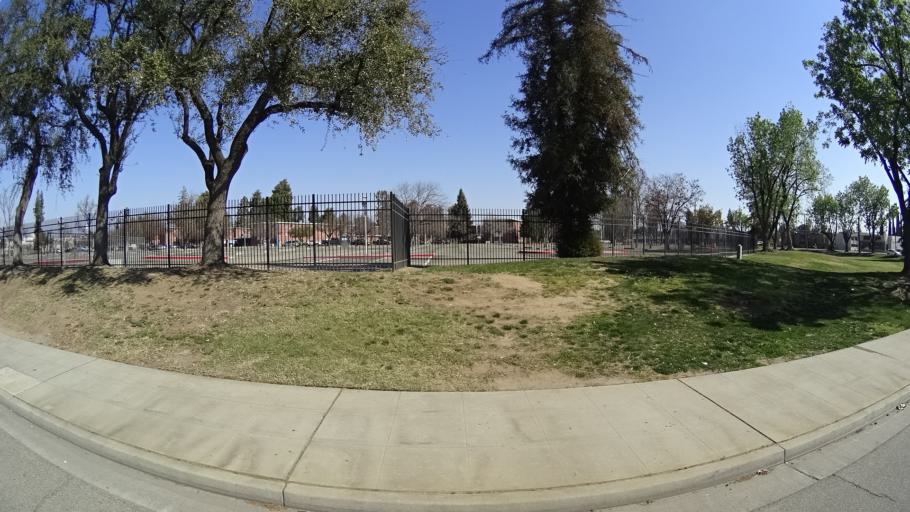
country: US
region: California
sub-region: Fresno County
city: Clovis
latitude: 36.8095
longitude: -119.7541
